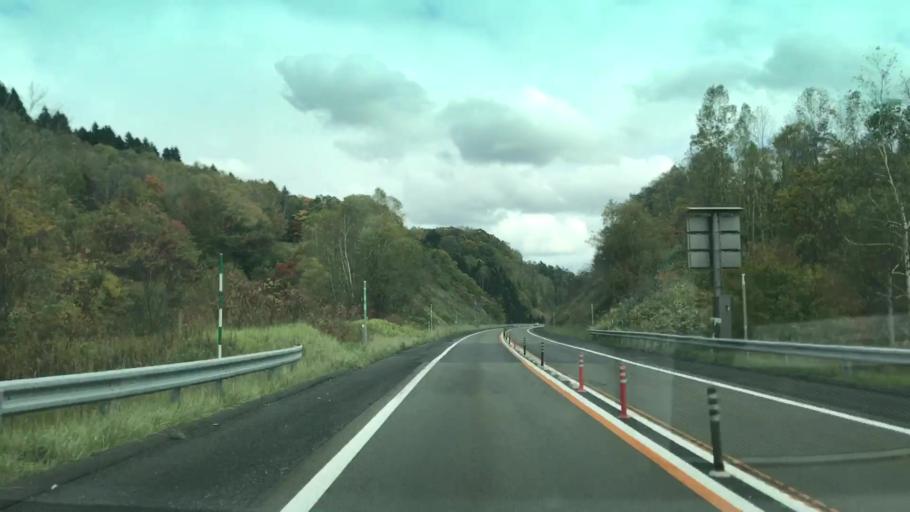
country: JP
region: Hokkaido
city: Chitose
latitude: 42.9152
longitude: 141.9684
